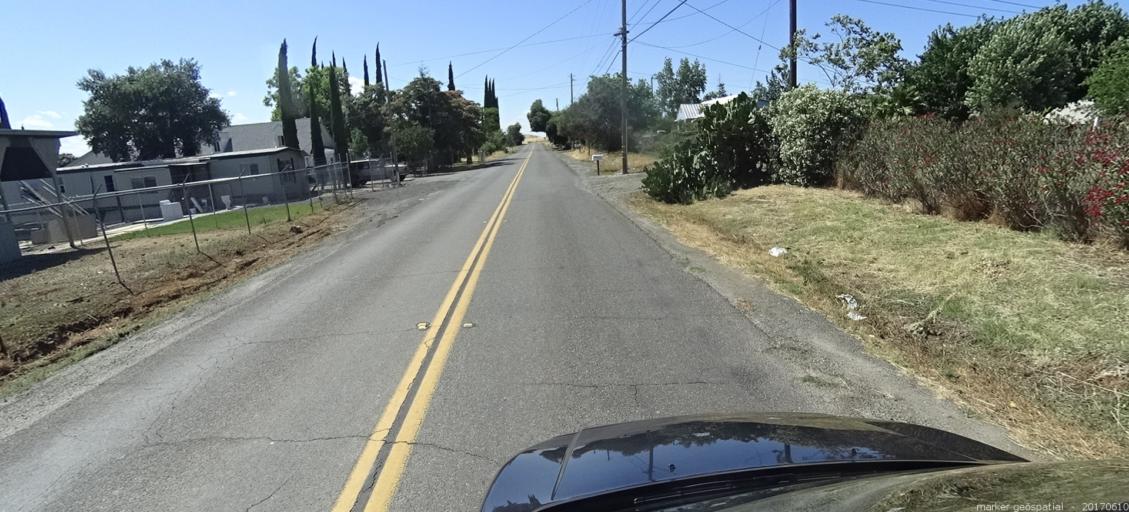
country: US
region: California
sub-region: Butte County
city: Thermalito
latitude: 39.5356
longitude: -121.5774
